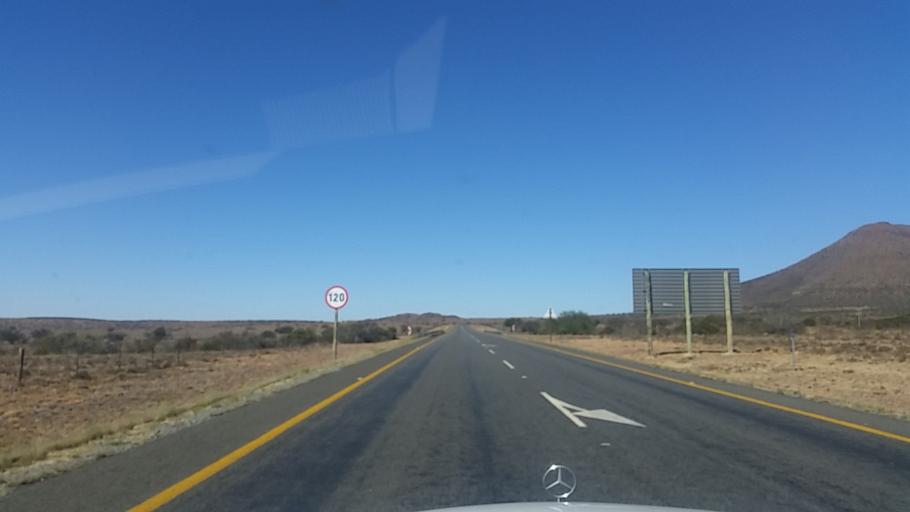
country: ZA
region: Eastern Cape
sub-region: Cacadu District Municipality
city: Graaff-Reinet
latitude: -32.0330
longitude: 24.6247
